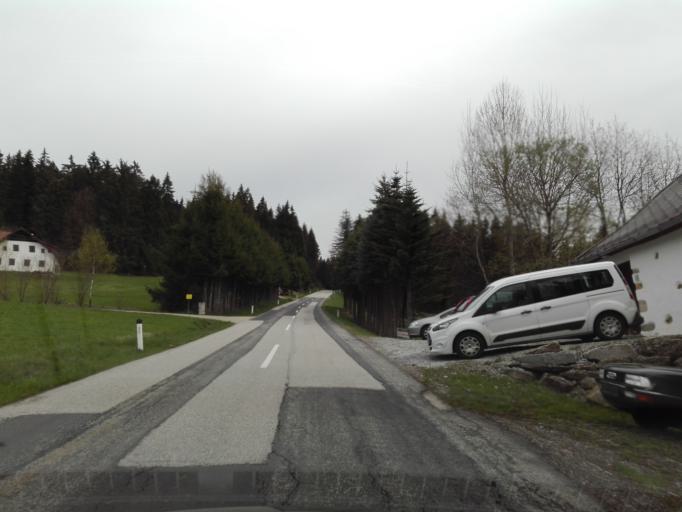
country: AT
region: Upper Austria
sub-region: Politischer Bezirk Rohrbach
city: Ulrichsberg
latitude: 48.6956
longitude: 13.9221
